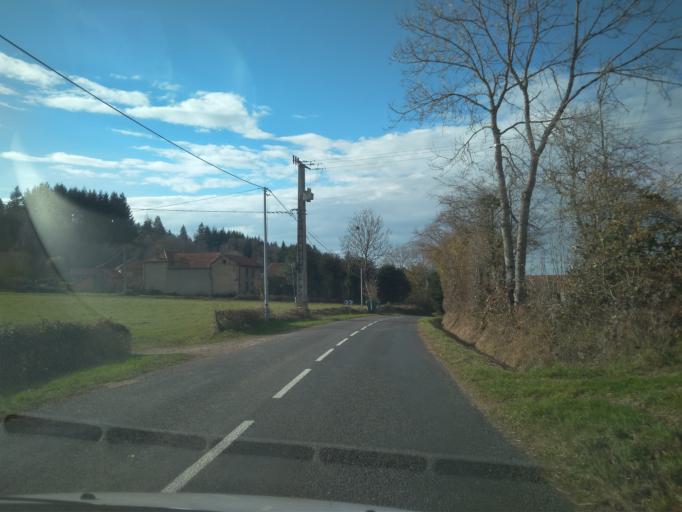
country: FR
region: Auvergne
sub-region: Departement de l'Allier
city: Le Mayet-de-Montagne
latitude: 46.1394
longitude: 3.7536
